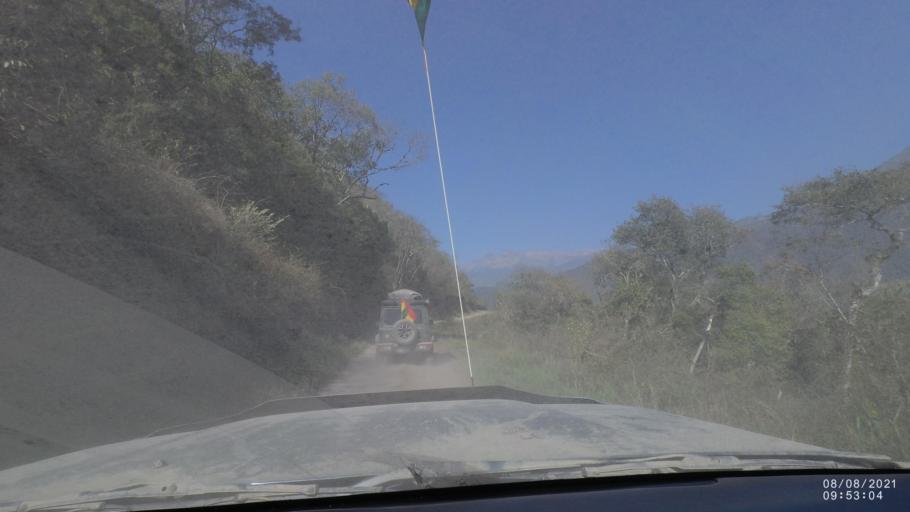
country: BO
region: La Paz
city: Quime
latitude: -16.6270
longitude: -66.7319
